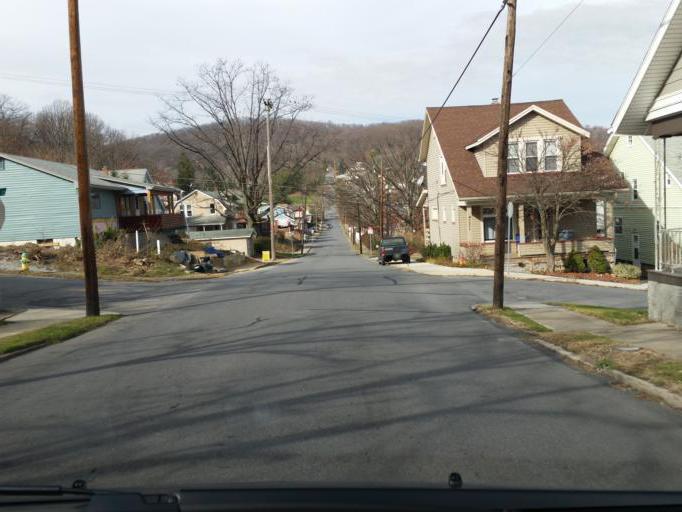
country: US
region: Pennsylvania
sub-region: Blair County
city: Altoona
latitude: 40.5207
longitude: -78.4093
